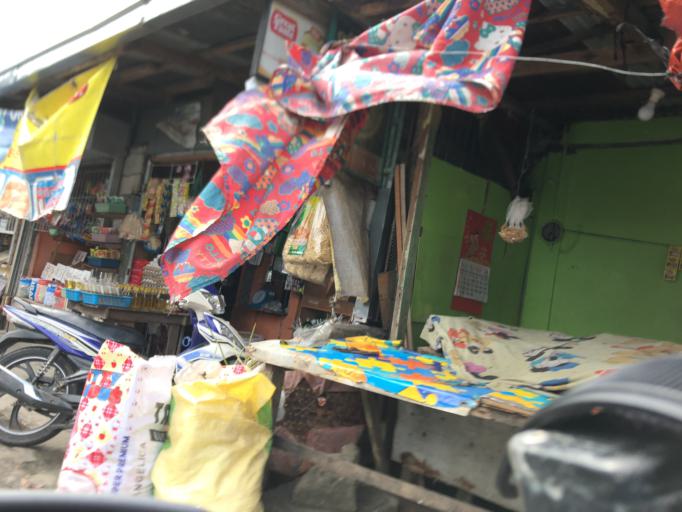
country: PH
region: Central Luzon
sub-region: Province of Bulacan
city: San Jose del Monte
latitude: 14.7675
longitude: 121.0531
